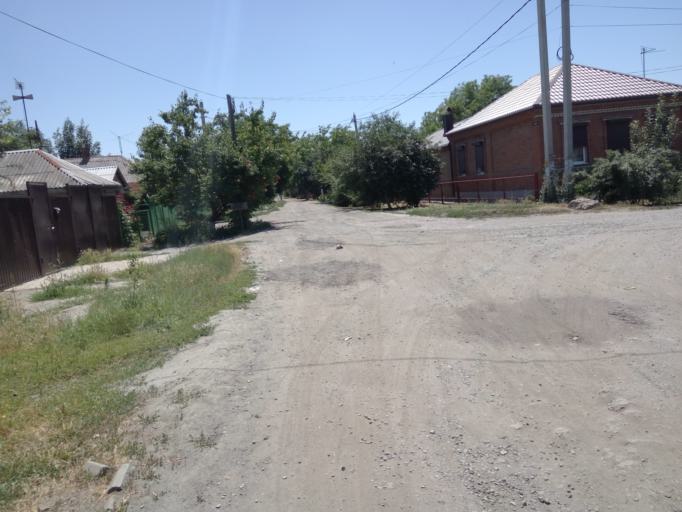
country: RU
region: Rostov
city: Bataysk
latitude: 47.1460
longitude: 39.7707
